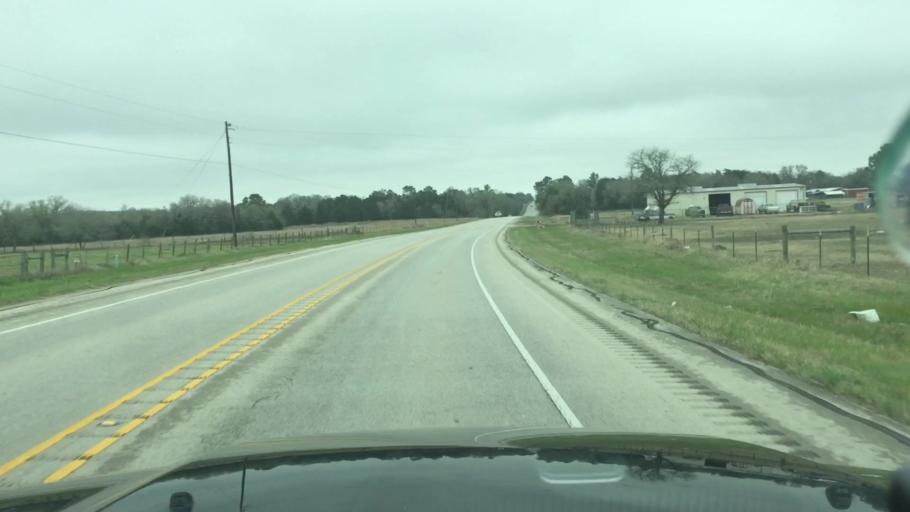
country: US
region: Texas
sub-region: Lee County
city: Giddings
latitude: 30.0637
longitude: -96.9162
